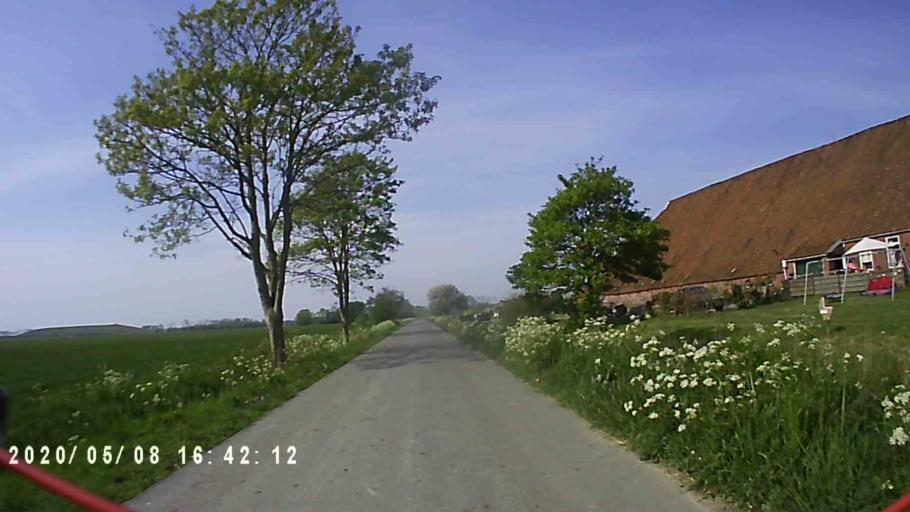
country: NL
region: Groningen
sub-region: Gemeente Bedum
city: Bedum
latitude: 53.3761
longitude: 6.6038
